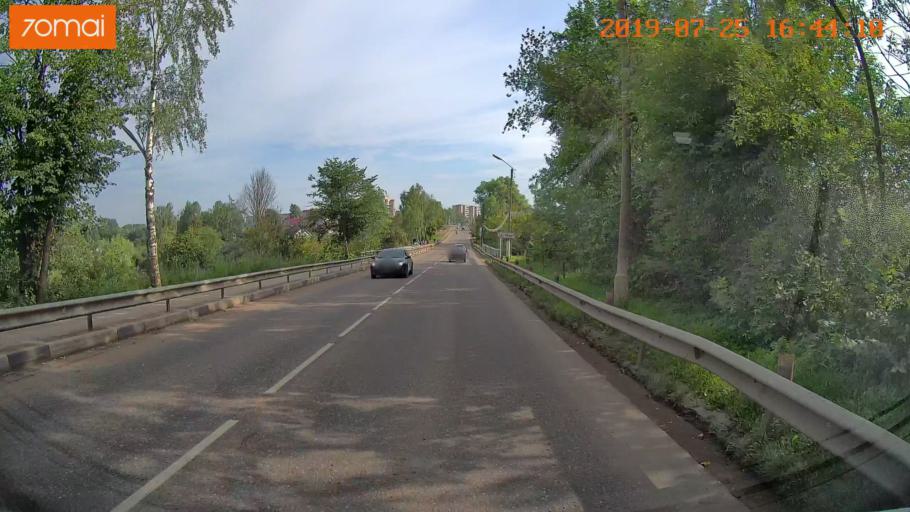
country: RU
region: Ivanovo
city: Privolzhsk
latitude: 57.3776
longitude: 41.2796
